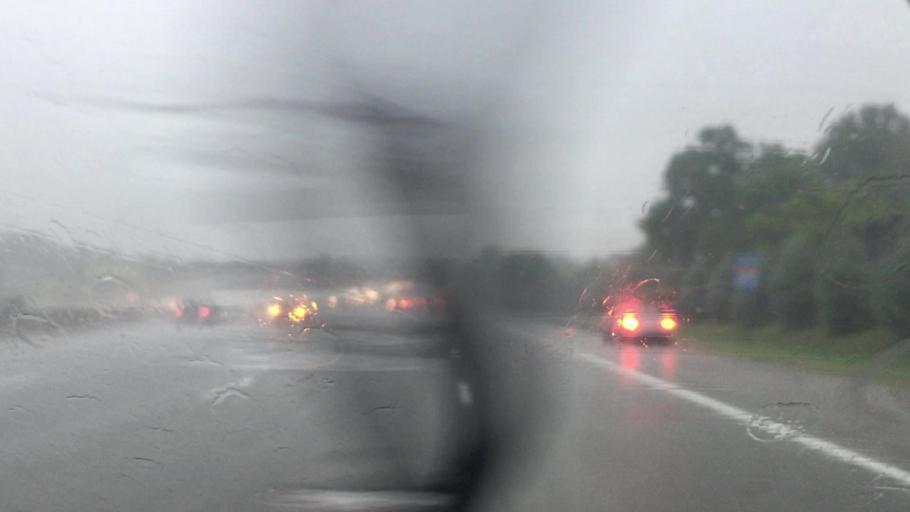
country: US
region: North Carolina
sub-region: Rowan County
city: Salisbury
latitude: 35.6527
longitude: -80.4674
